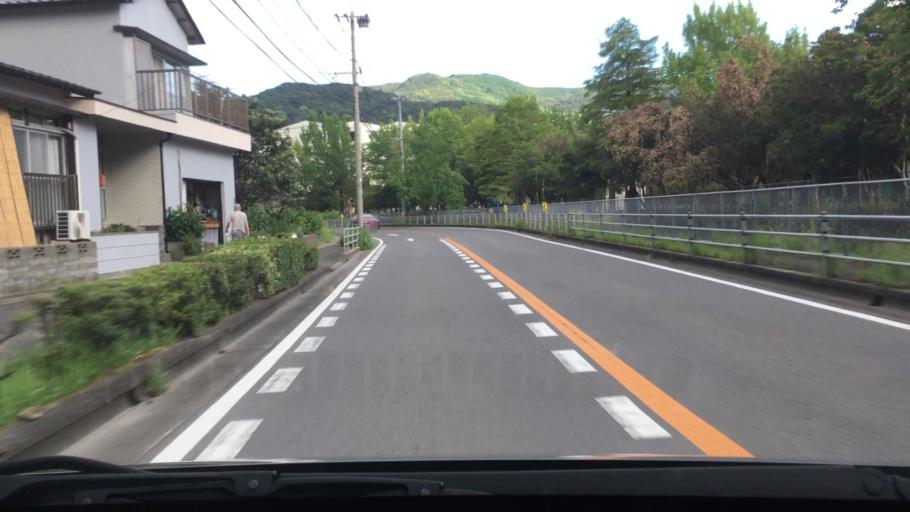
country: JP
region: Nagasaki
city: Togitsu
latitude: 32.8261
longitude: 129.7734
